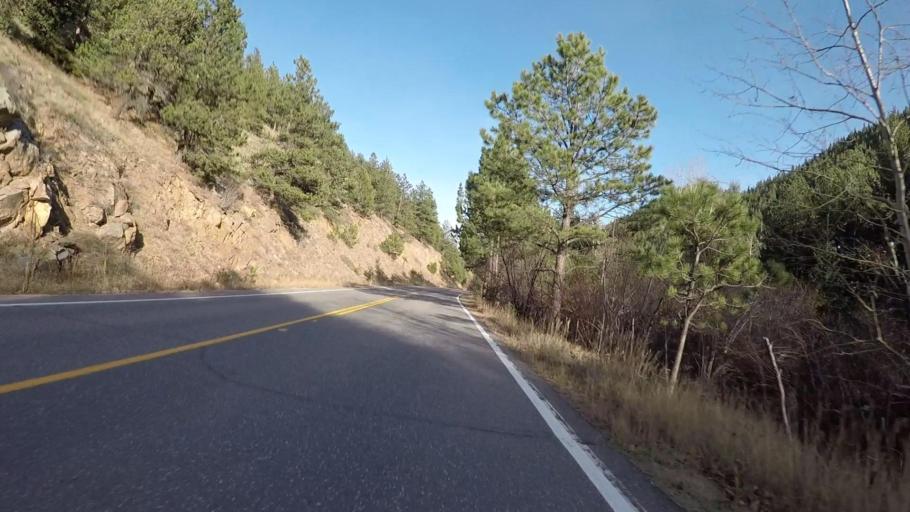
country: US
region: Colorado
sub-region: Boulder County
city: Nederland
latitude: 40.0682
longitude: -105.4412
